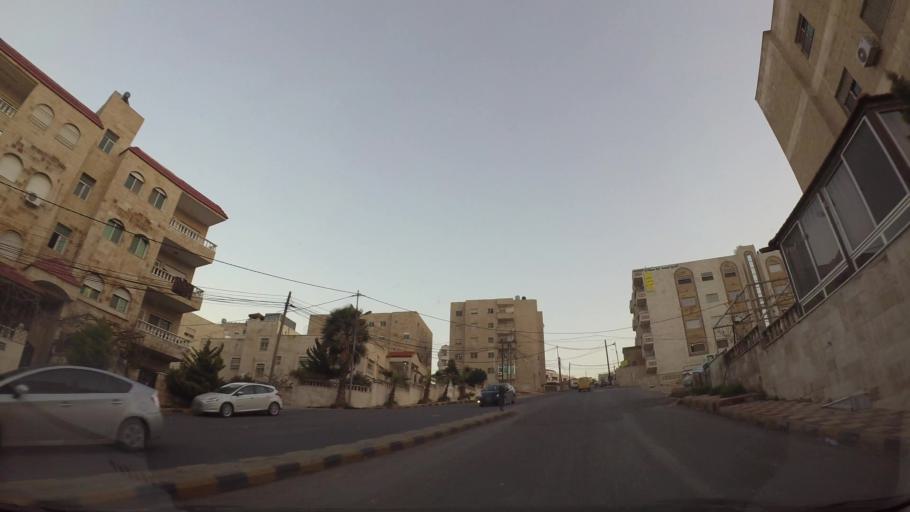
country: JO
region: Amman
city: Amman
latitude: 31.9918
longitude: 35.9563
